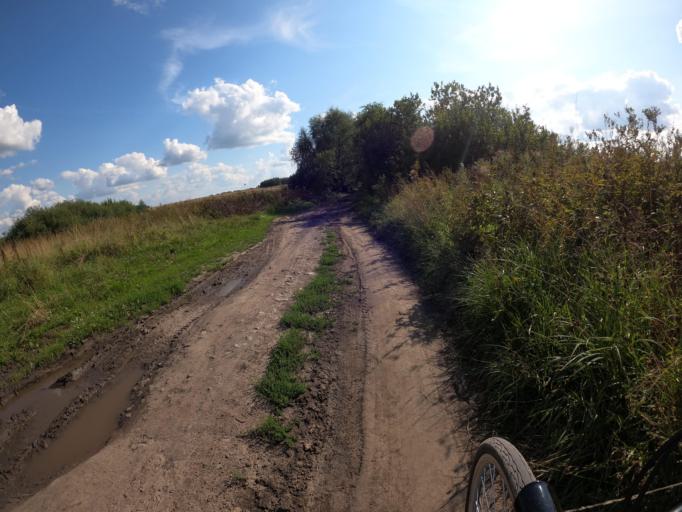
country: RU
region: Moskovskaya
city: Troitskoye
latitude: 55.2313
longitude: 38.4861
